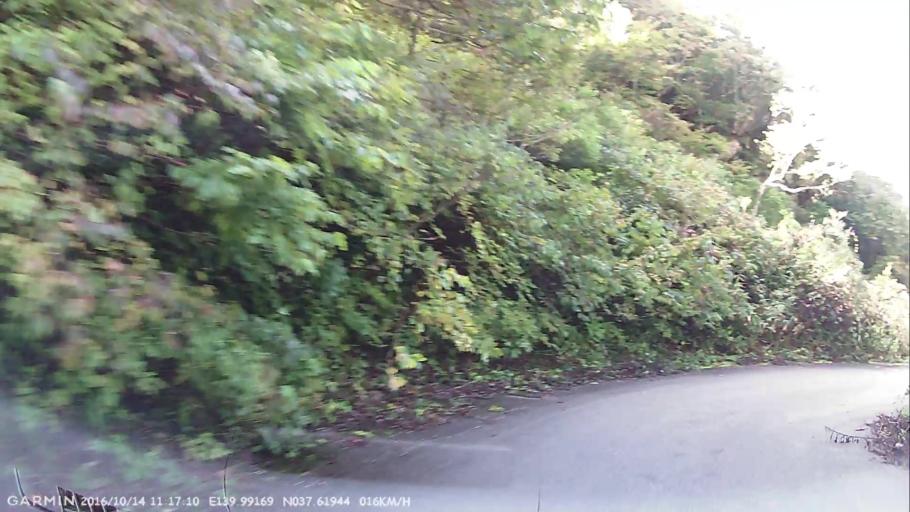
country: JP
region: Fukushima
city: Kitakata
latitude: 37.6194
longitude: 139.9917
